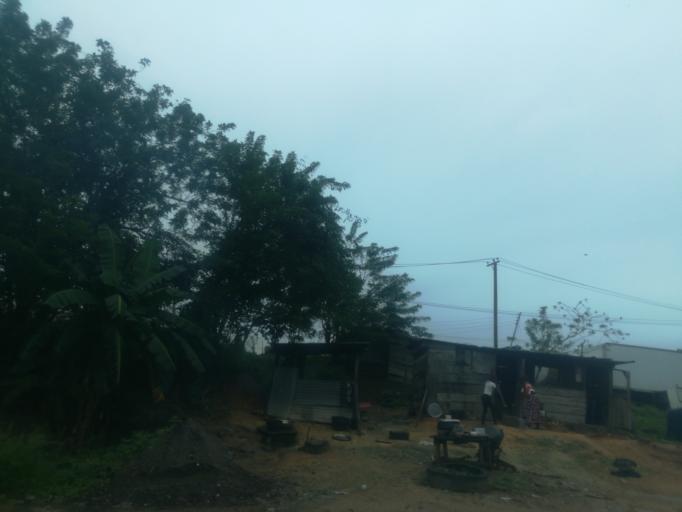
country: NG
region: Oyo
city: Ibadan
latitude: 7.3331
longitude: 3.8824
